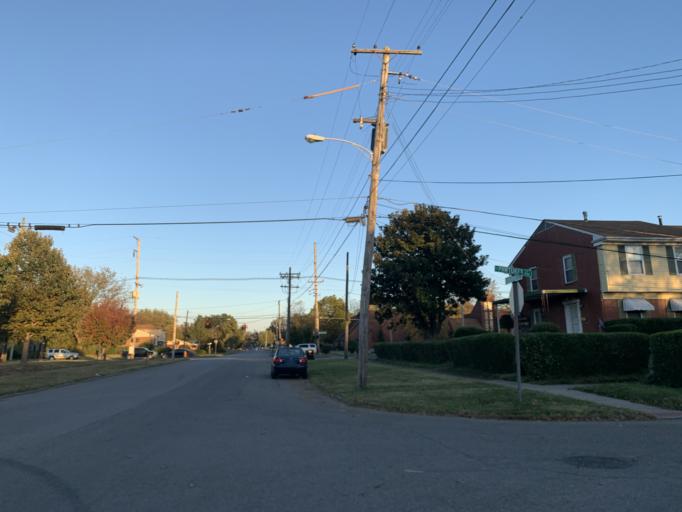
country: US
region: Kentucky
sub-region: Jefferson County
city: Shively
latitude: 38.2324
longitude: -85.8126
